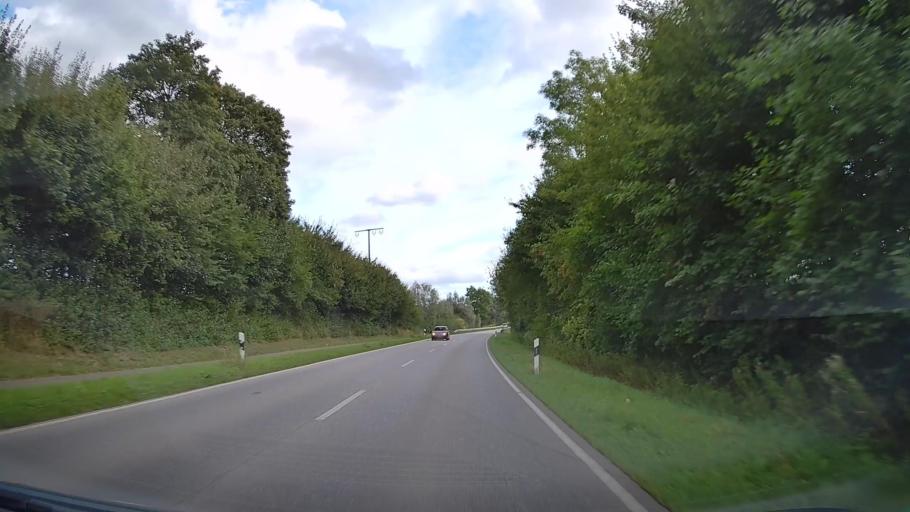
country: DE
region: Schleswig-Holstein
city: Niesgrau
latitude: 54.7556
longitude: 9.8051
